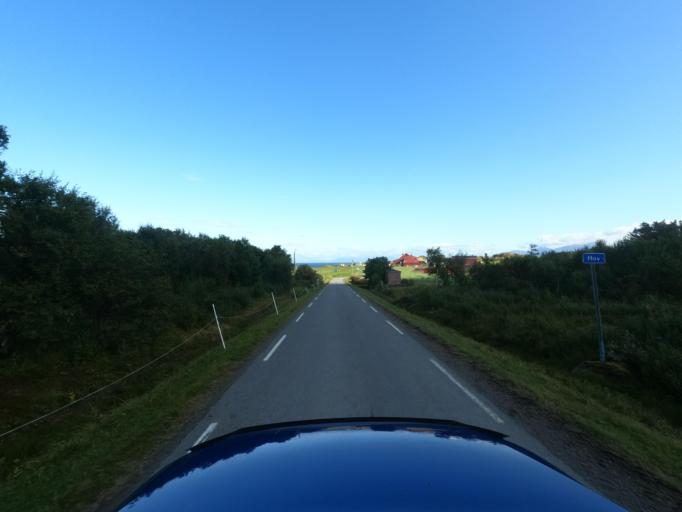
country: NO
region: Nordland
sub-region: Vestvagoy
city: Evjen
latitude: 68.3369
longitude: 14.1046
